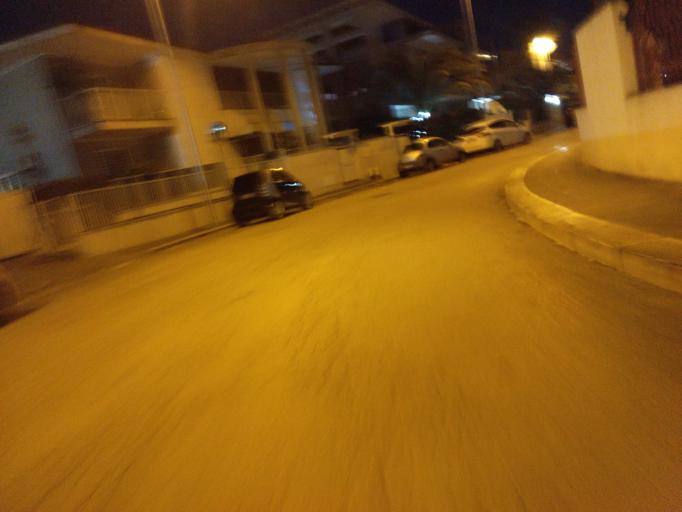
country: IT
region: Apulia
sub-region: Provincia di Bari
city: Modugno
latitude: 41.0806
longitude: 16.7900
